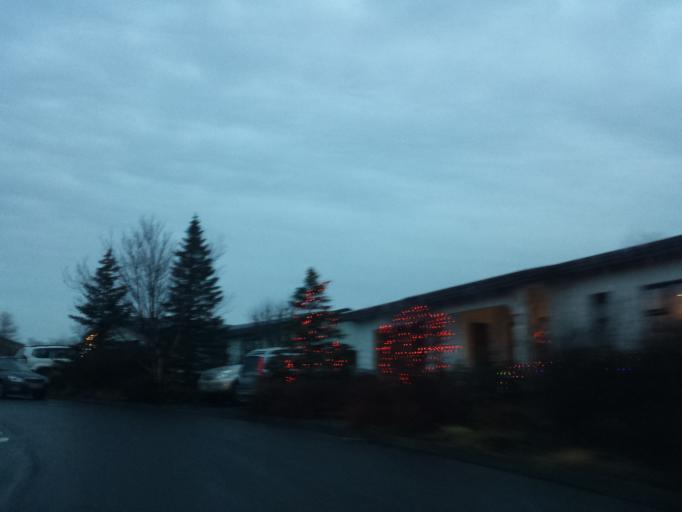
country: IS
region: Capital Region
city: Mosfellsbaer
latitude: 64.1348
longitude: -21.7741
